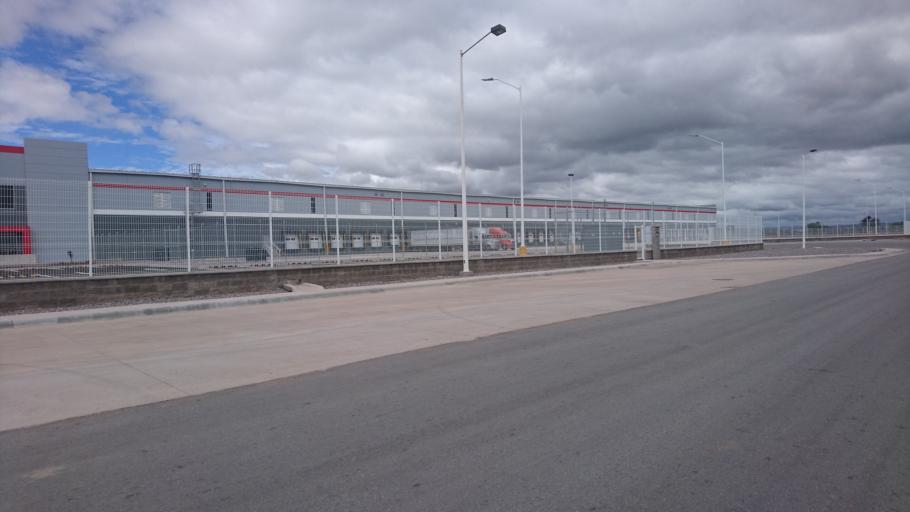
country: MX
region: San Luis Potosi
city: La Pila
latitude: 21.9925
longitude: -100.8591
